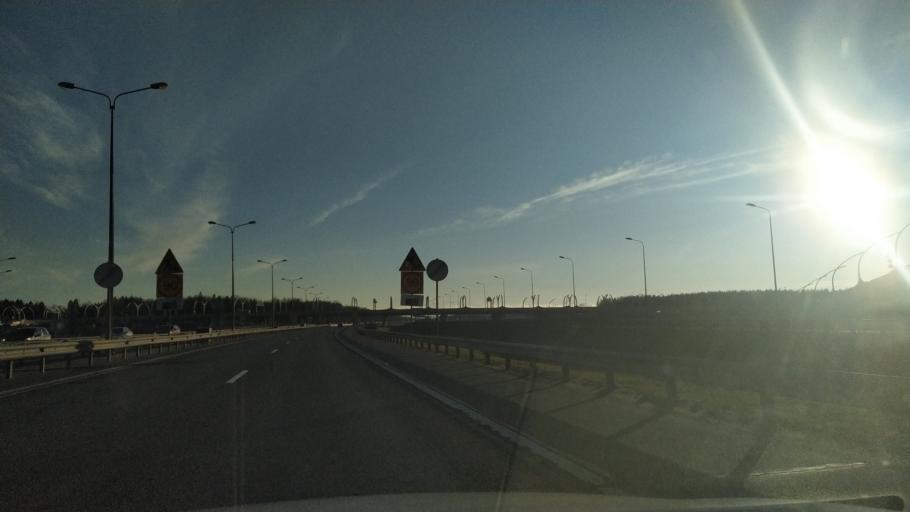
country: RU
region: St.-Petersburg
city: Ol'gino
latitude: 60.0602
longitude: 30.1511
